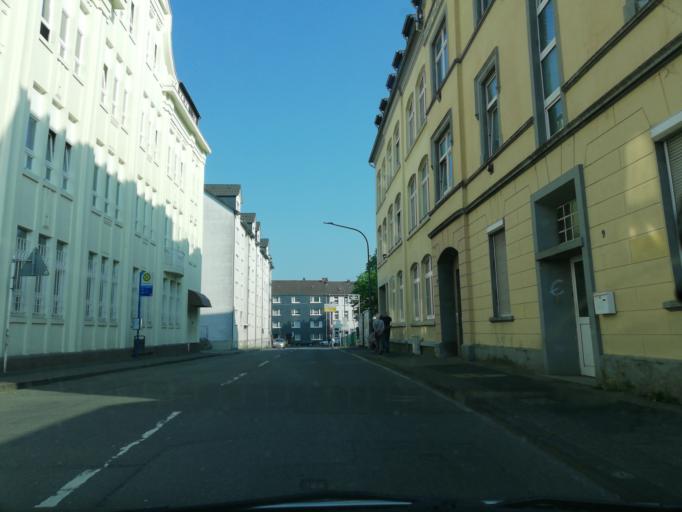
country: DE
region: North Rhine-Westphalia
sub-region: Regierungsbezirk Arnsberg
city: Schwelm
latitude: 51.2720
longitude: 7.2374
